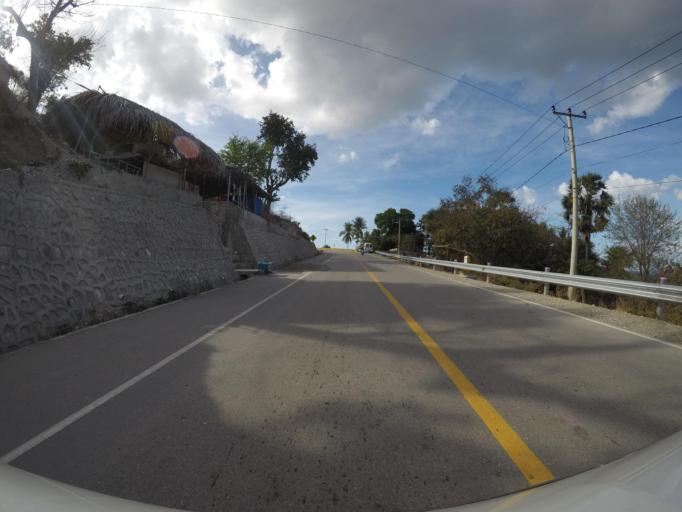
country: TL
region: Baucau
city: Baucau
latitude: -8.4679
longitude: 126.4845
